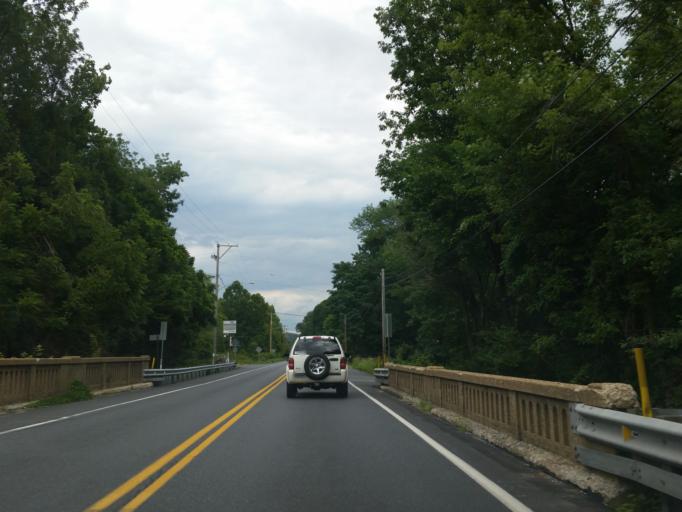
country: US
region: Pennsylvania
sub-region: Lancaster County
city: Adamstown
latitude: 40.2423
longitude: -76.0539
